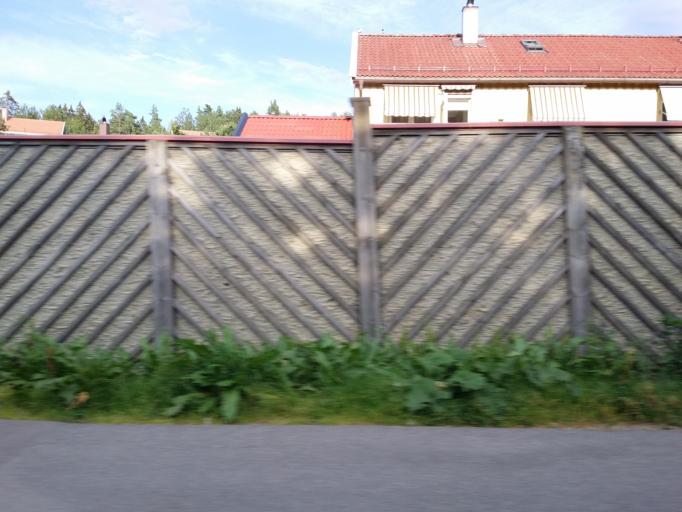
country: NO
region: Akershus
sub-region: Lorenskog
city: Kjenn
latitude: 59.9054
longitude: 10.8514
